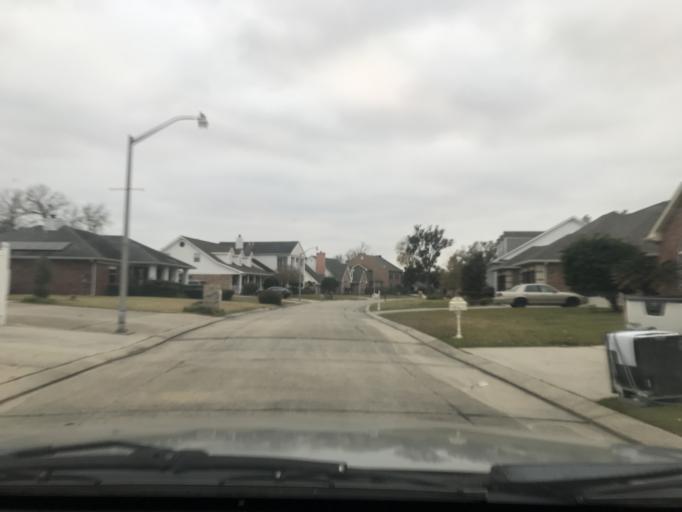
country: US
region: Louisiana
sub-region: Jefferson Parish
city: Woodmere
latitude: 29.8706
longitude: -90.0893
